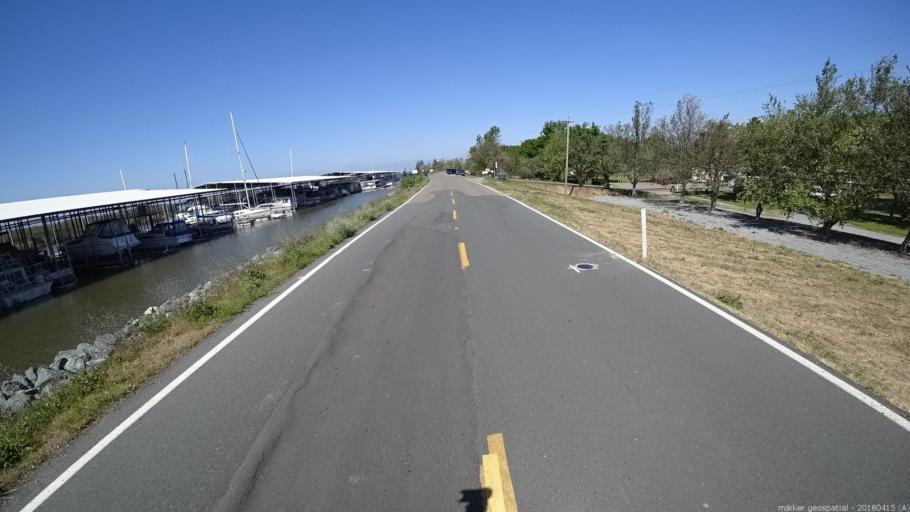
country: US
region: California
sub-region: Contra Costa County
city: Bethel Island
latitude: 38.1082
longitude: -121.6009
